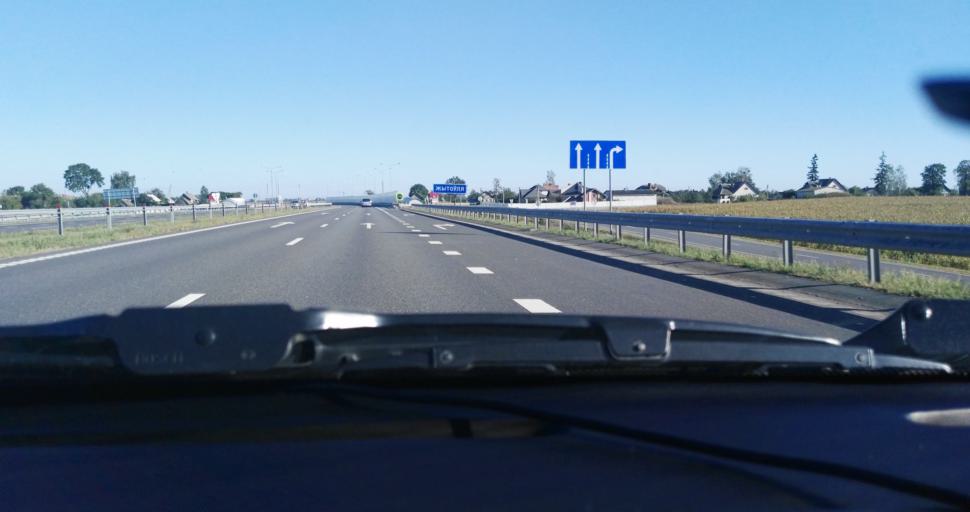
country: BY
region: Gomel
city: Buda-Kashalyova
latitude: 52.5165
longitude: 30.6284
